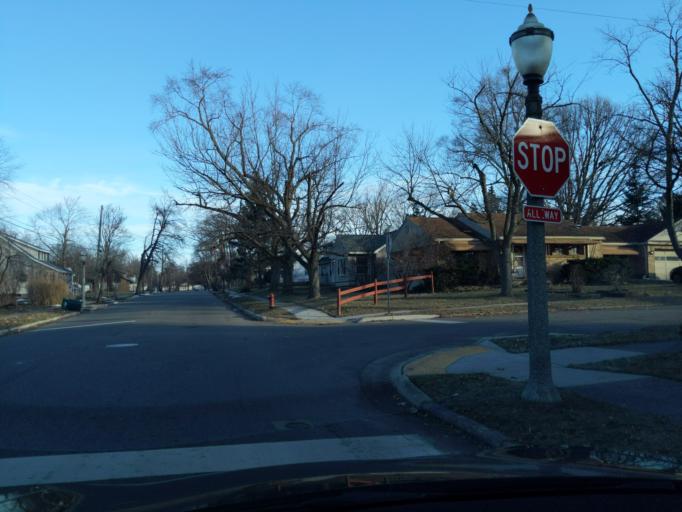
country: US
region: Michigan
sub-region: Ingham County
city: Lansing
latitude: 42.6943
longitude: -84.5619
